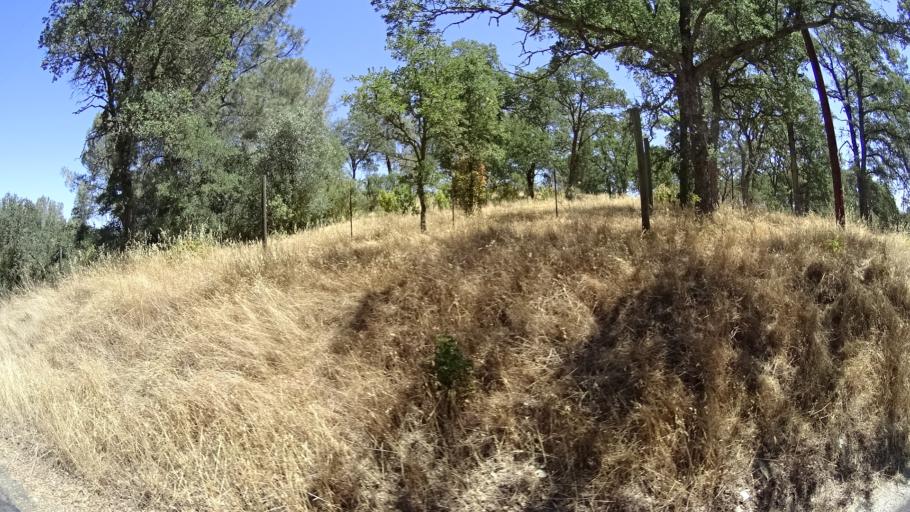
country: US
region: California
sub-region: Calaveras County
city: Copperopolis
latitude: 37.9671
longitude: -120.6907
